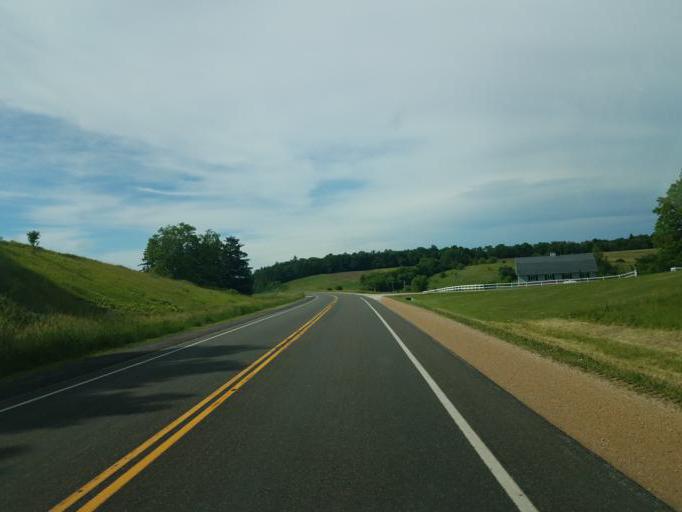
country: US
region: Wisconsin
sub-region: Monroe County
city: Tomah
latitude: 43.9164
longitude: -90.4948
